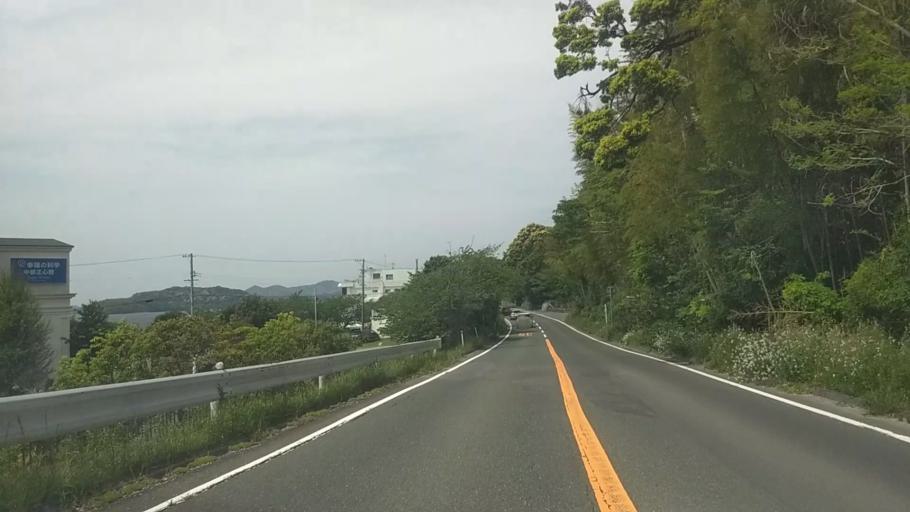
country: JP
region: Shizuoka
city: Kosai-shi
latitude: 34.7681
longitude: 137.5537
